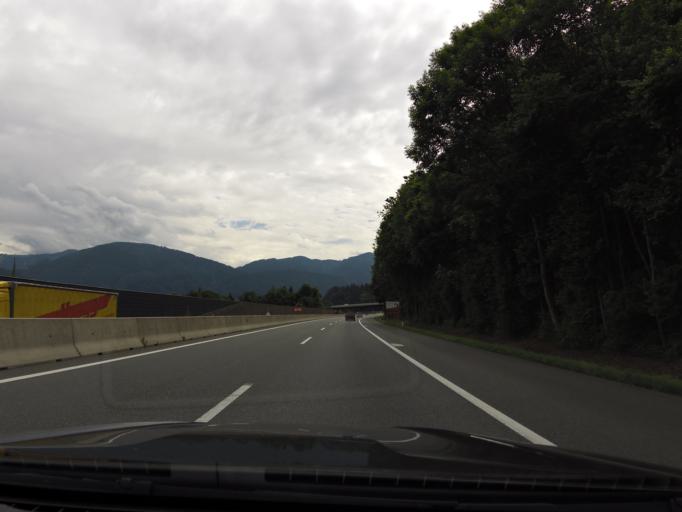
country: AT
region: Tyrol
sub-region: Politischer Bezirk Kufstein
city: Angath
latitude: 47.5111
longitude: 12.0633
